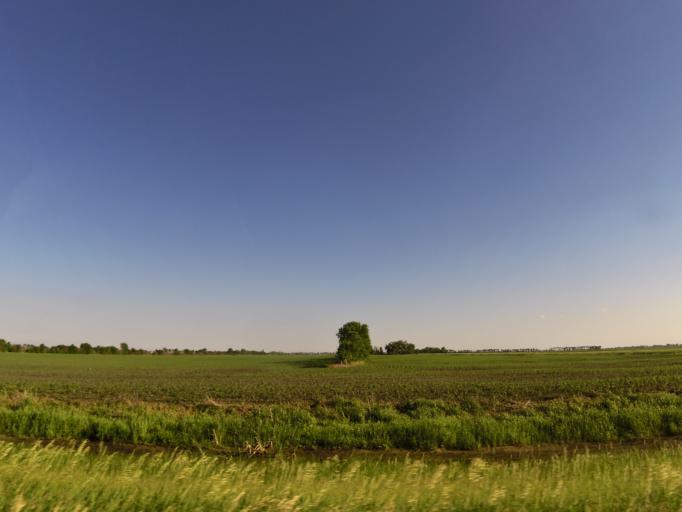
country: US
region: North Dakota
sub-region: Grand Forks County
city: Grand Forks Air Force Base
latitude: 48.1357
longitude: -97.2333
